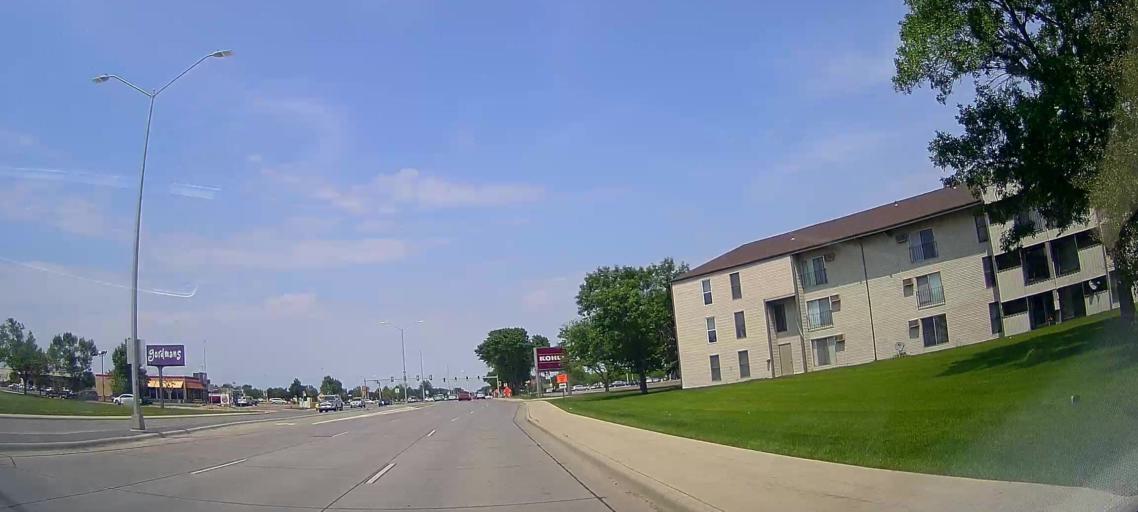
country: US
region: South Dakota
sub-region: Minnehaha County
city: Sioux Falls
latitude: 43.5088
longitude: -96.7708
